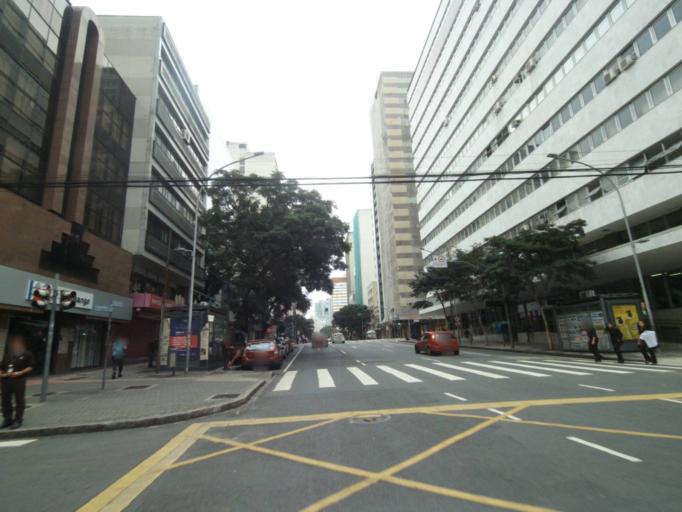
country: BR
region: Parana
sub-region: Curitiba
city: Curitiba
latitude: -25.4302
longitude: -49.2667
